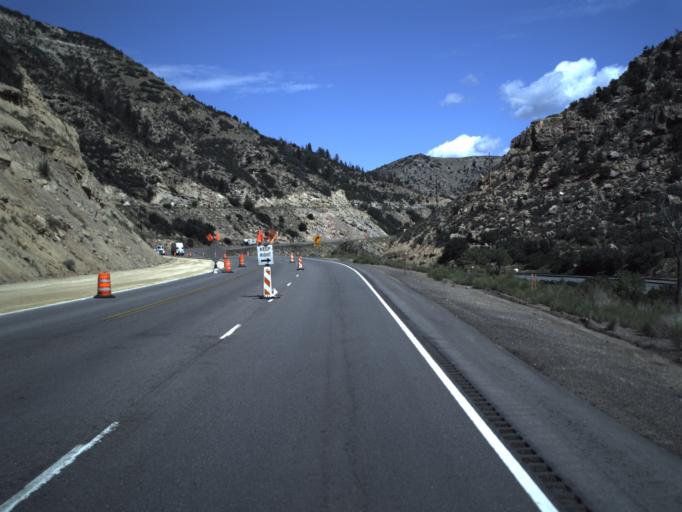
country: US
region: Utah
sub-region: Carbon County
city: Helper
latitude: 39.7878
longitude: -110.9287
